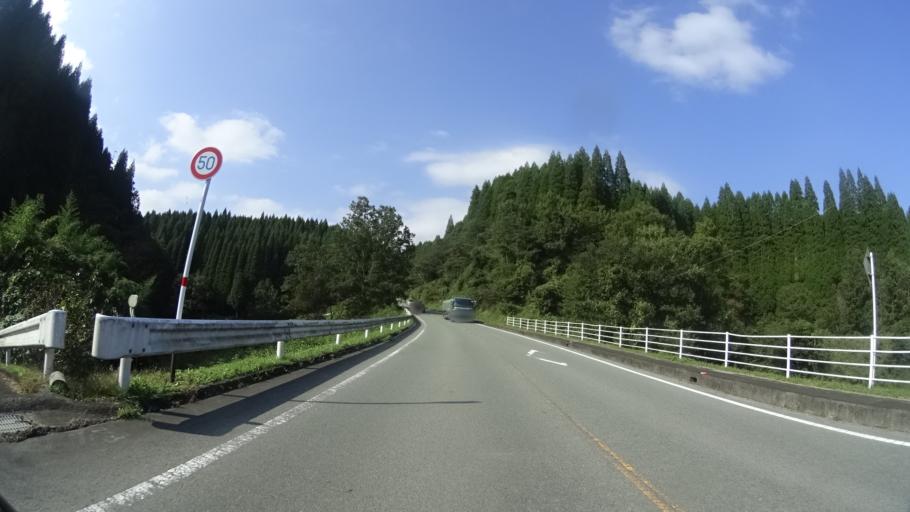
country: JP
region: Oita
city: Tsukawaki
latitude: 33.1314
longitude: 131.0876
